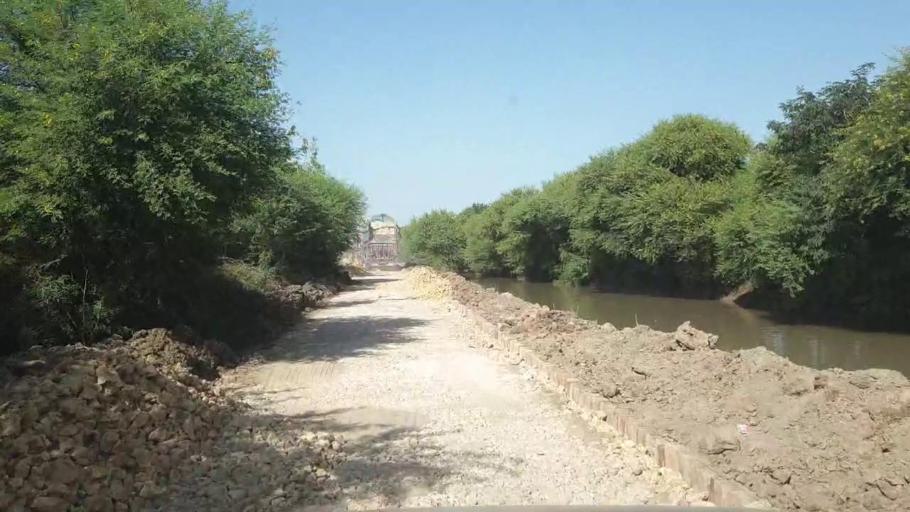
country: PK
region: Sindh
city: Kadhan
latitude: 24.5325
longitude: 69.0013
